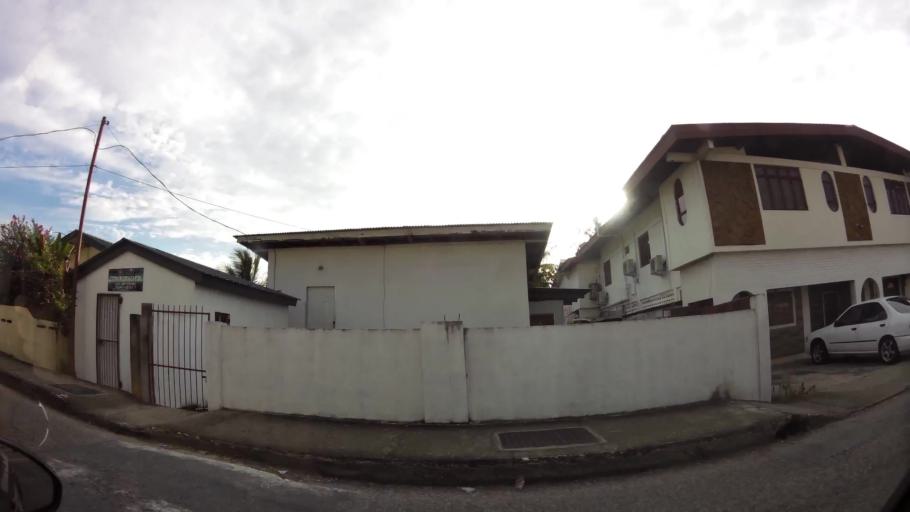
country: TT
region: Tunapuna/Piarco
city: Tunapuna
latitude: 10.6401
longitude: -61.4027
